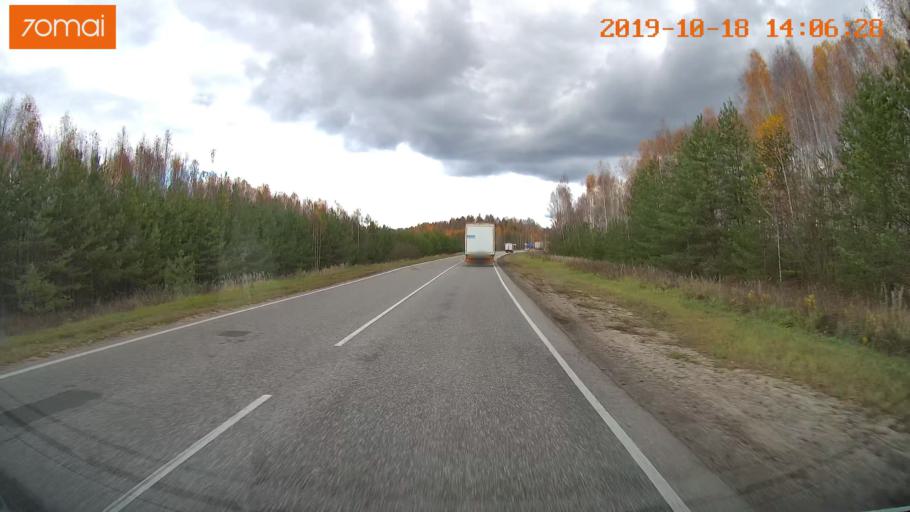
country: RU
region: Rjazan
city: Spas-Klepiki
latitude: 55.1455
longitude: 40.1502
